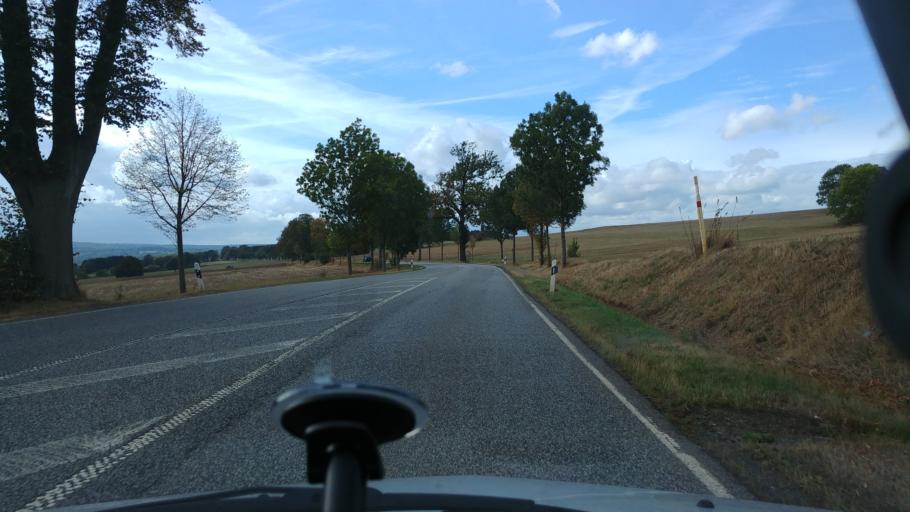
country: DE
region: Hesse
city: Herbstein
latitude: 50.5380
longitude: 9.3783
